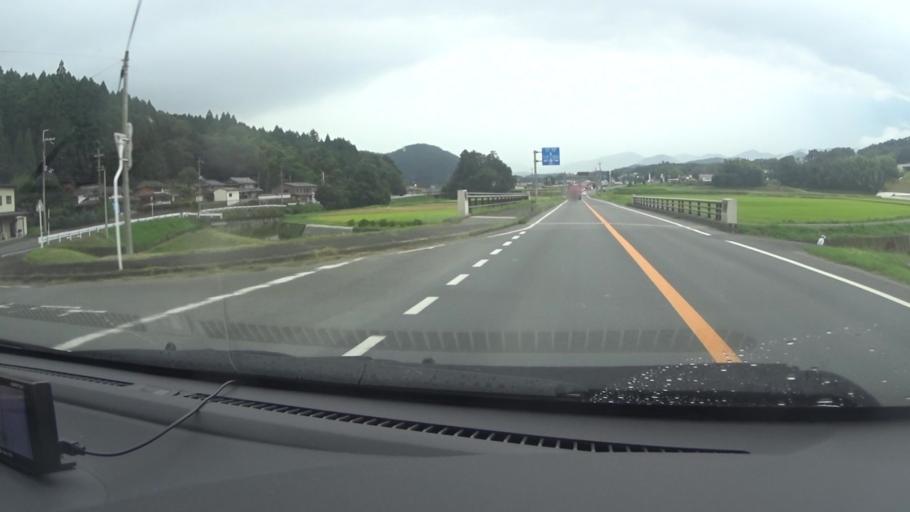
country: JP
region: Kyoto
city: Ayabe
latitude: 35.1855
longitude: 135.3658
